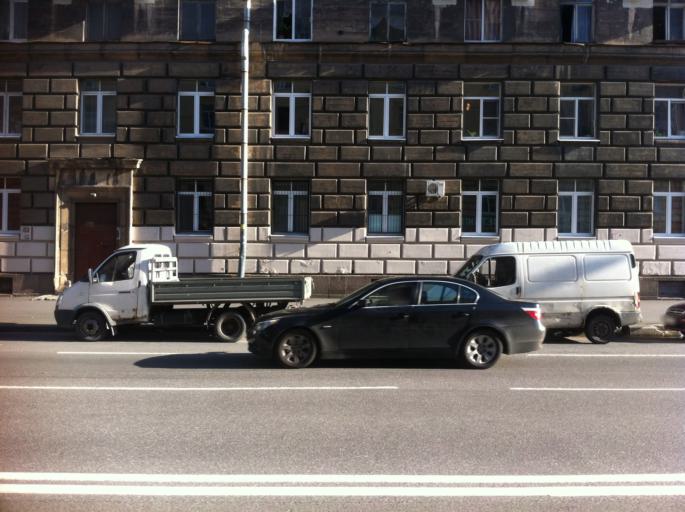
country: RU
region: St.-Petersburg
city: Avtovo
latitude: 59.8699
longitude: 30.2579
